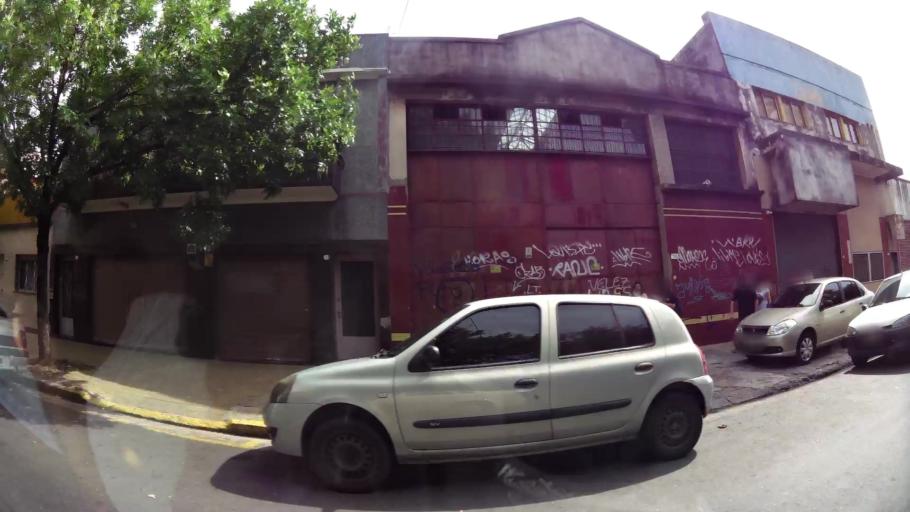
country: AR
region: Buenos Aires F.D.
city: Villa Santa Rita
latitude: -34.6444
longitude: -58.4976
